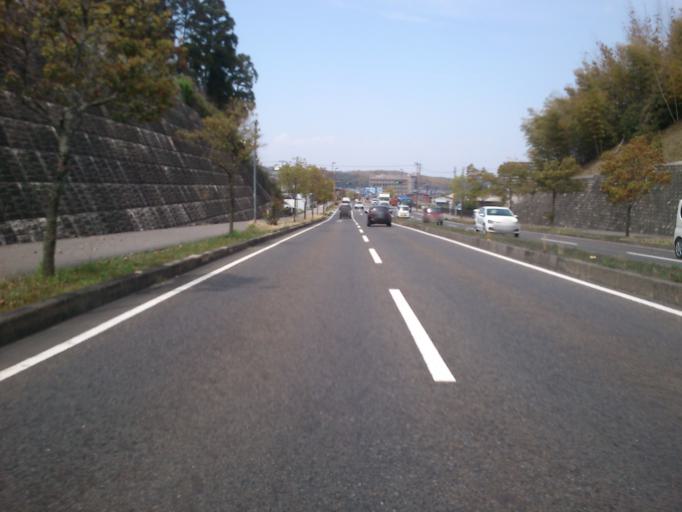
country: JP
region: Kyoto
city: Tanabe
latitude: 34.7544
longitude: 135.7872
